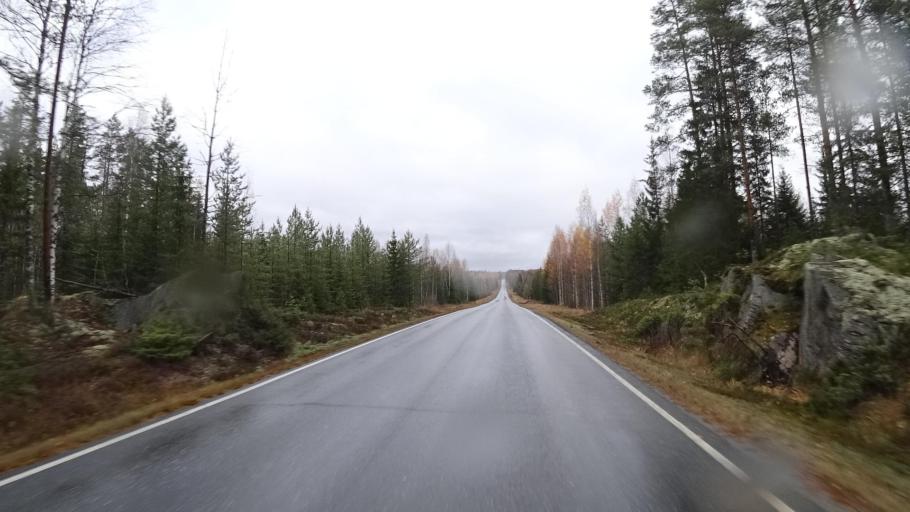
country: FI
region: North Karelia
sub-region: Joensuu
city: Polvijaervi
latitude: 63.0859
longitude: 29.5877
